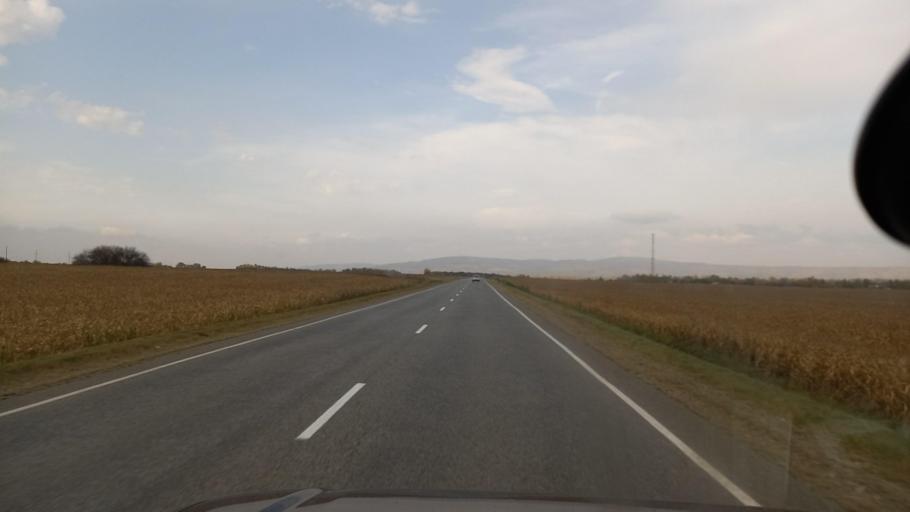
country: RU
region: Krasnodarskiy
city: Shedok
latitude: 44.2602
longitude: 40.8676
